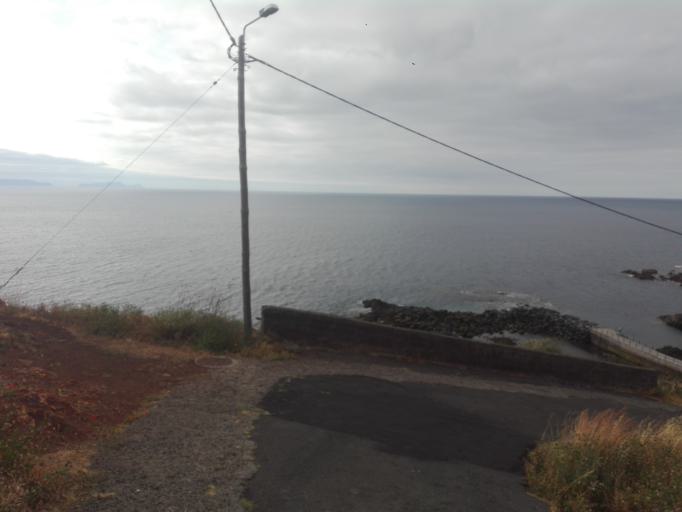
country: PT
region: Madeira
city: Canico
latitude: 32.6484
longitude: -16.8239
